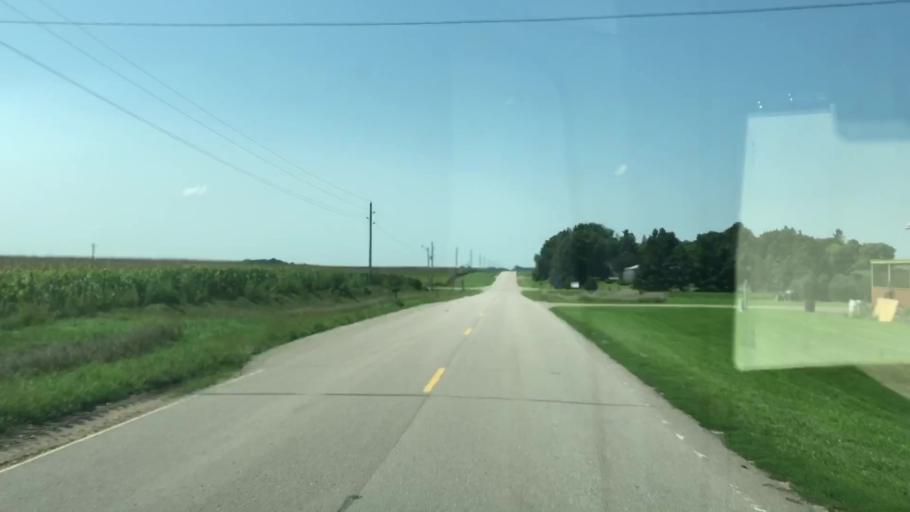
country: US
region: Iowa
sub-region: O'Brien County
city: Sheldon
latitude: 43.2443
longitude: -95.7811
